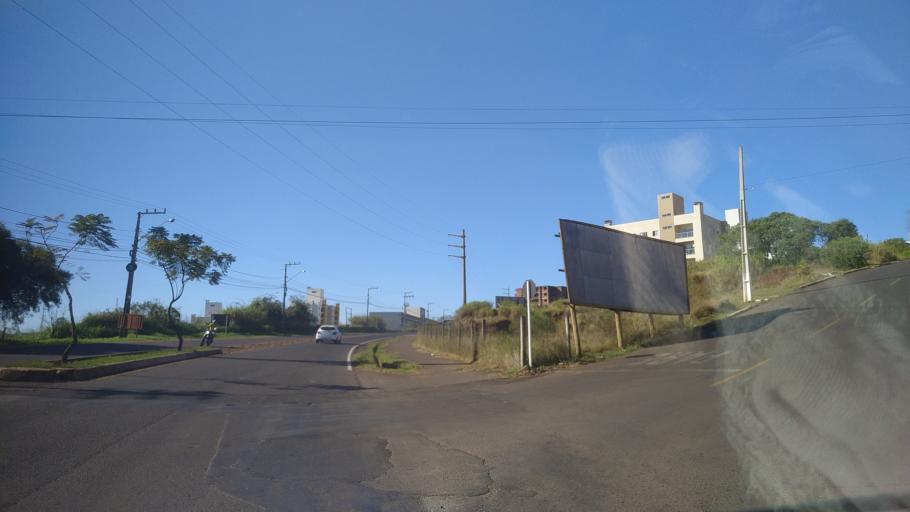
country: BR
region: Santa Catarina
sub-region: Chapeco
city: Chapeco
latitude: -27.1053
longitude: -52.5983
